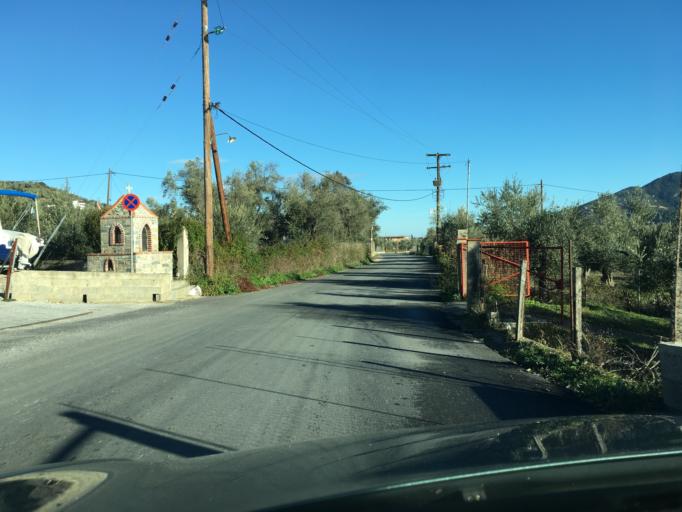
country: GR
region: Thessaly
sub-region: Nomos Magnisias
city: Skopelos
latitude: 39.1088
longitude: 23.7230
